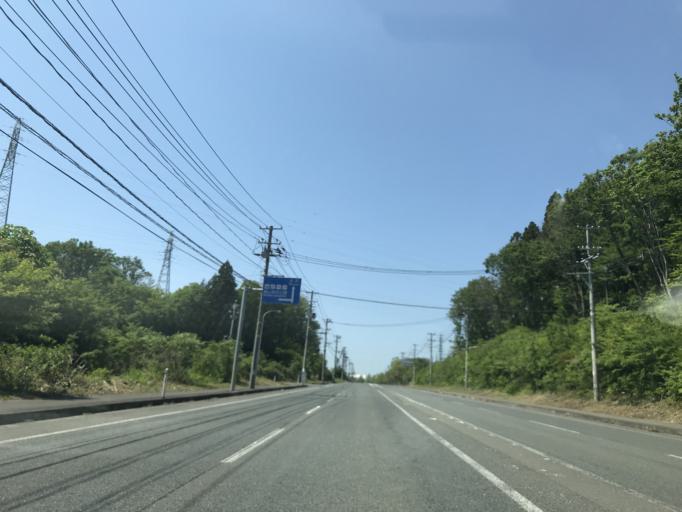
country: JP
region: Iwate
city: Kitakami
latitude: 39.2183
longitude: 141.0862
